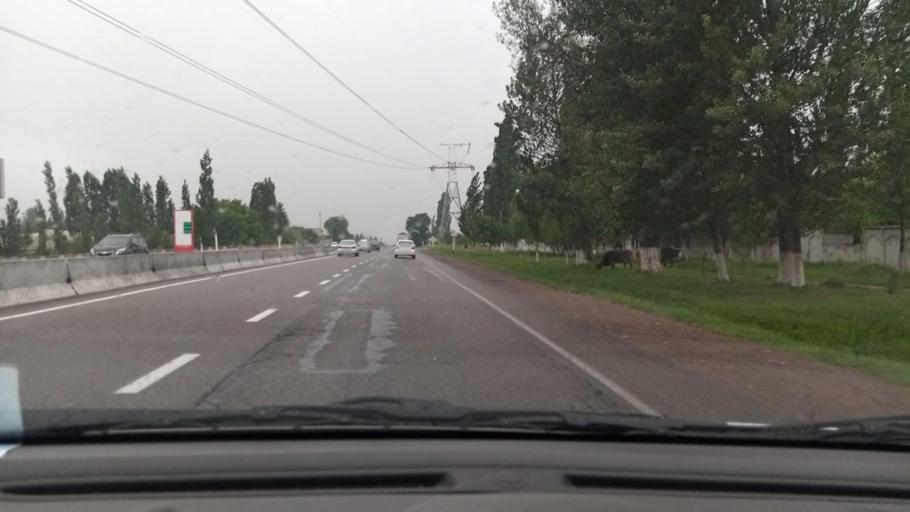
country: UZ
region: Toshkent
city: Angren
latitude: 40.9878
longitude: 70.0363
